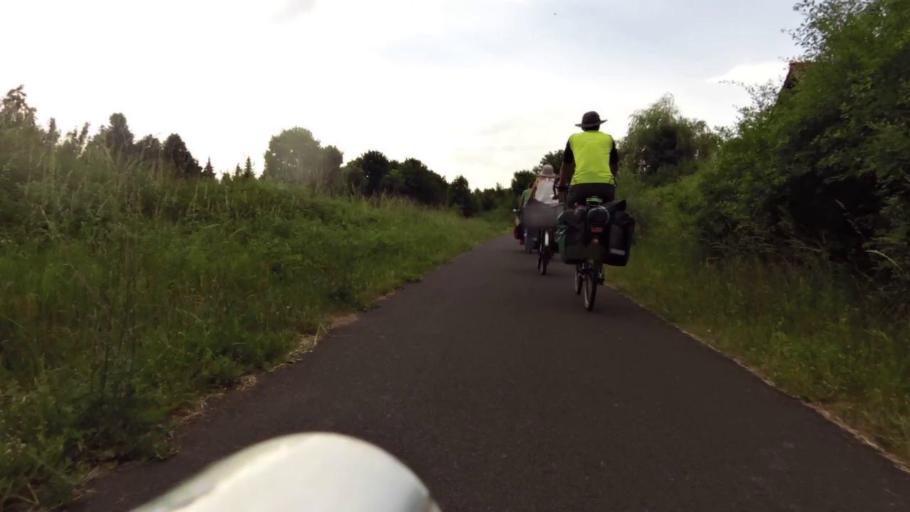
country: PL
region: Kujawsko-Pomorskie
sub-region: Powiat torunski
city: Lubianka
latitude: 53.1119
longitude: 18.4740
